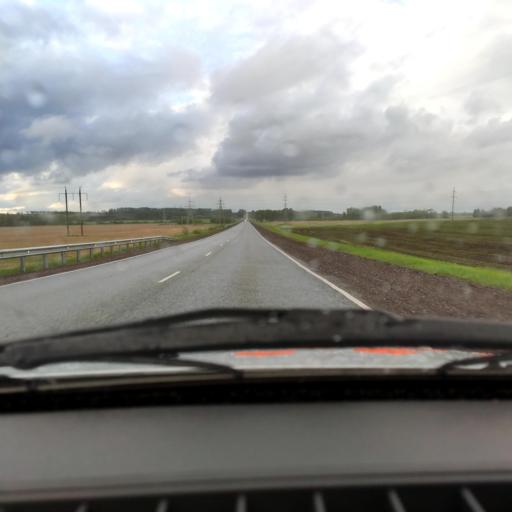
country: RU
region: Bashkortostan
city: Sterlitamak
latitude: 53.6679
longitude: 55.8523
